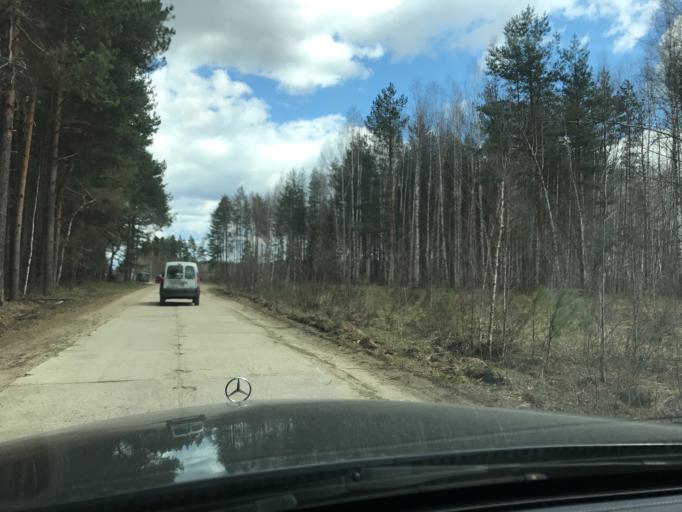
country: RU
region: Vladimir
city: Pokrov
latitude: 55.8712
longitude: 39.2383
